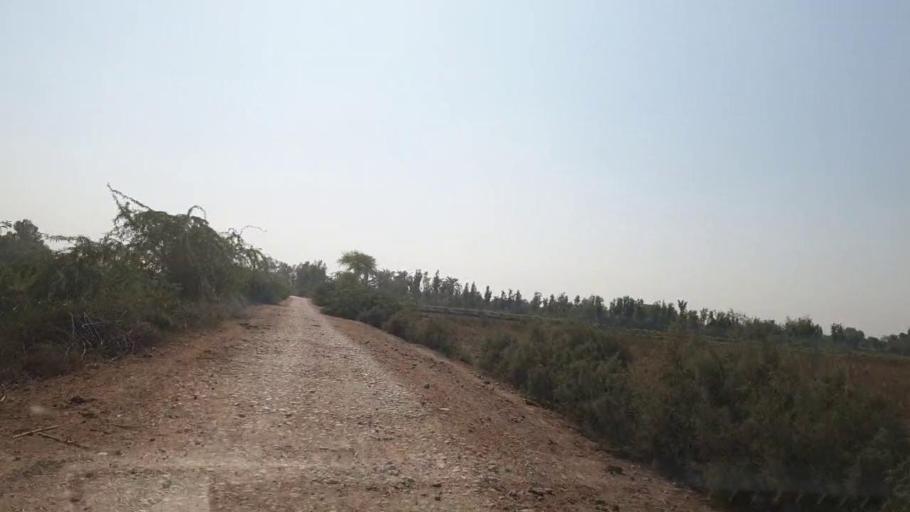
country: PK
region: Sindh
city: Gharo
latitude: 24.6806
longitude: 67.7496
